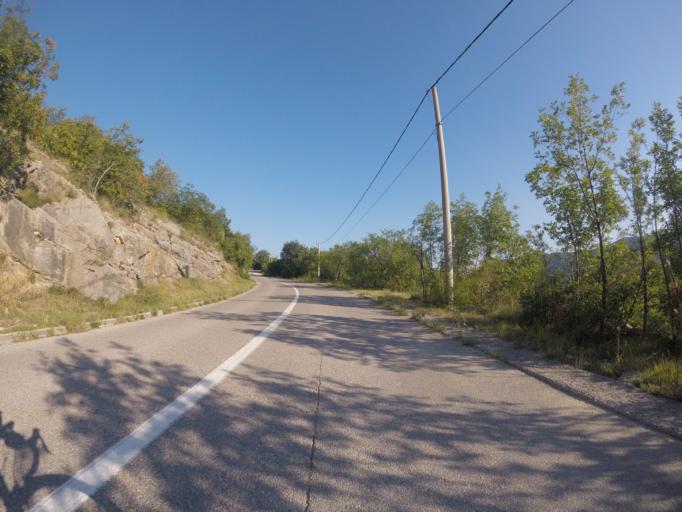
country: HR
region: Primorsko-Goranska
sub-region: Grad Crikvenica
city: Crikvenica
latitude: 45.2209
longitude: 14.6888
